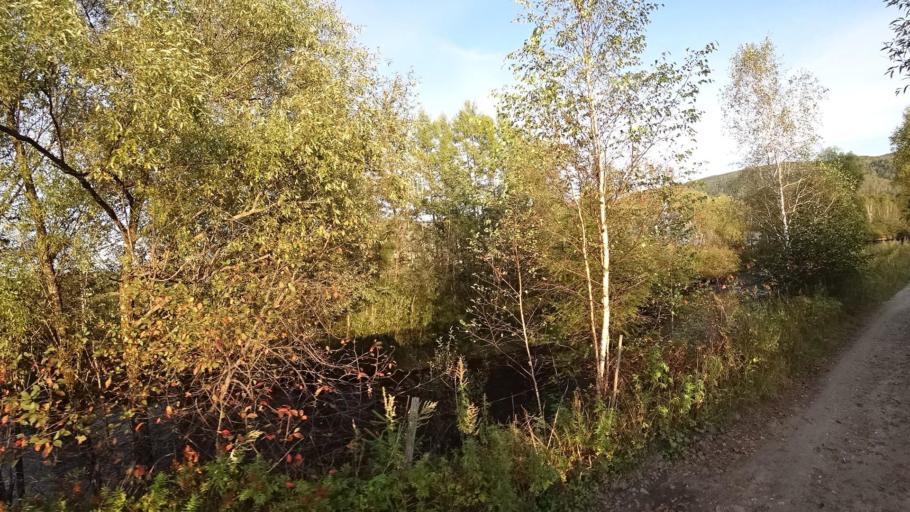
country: RU
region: Jewish Autonomous Oblast
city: Kul'dur
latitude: 49.2001
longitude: 131.6283
